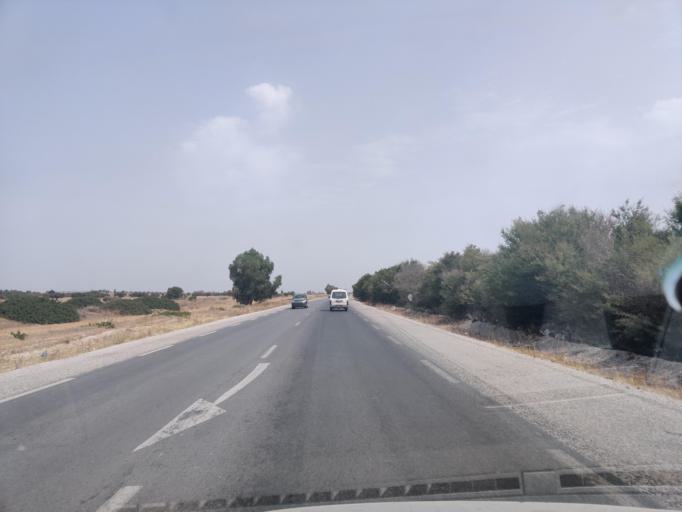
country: TN
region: Nabul
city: Bu `Urqub
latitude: 36.4827
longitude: 10.5718
